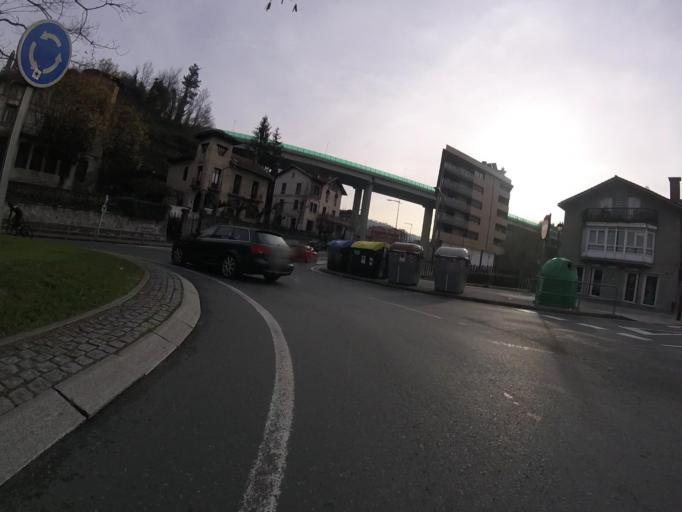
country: ES
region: Basque Country
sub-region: Provincia de Guipuzcoa
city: Tolosa
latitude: 43.1346
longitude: -2.0725
